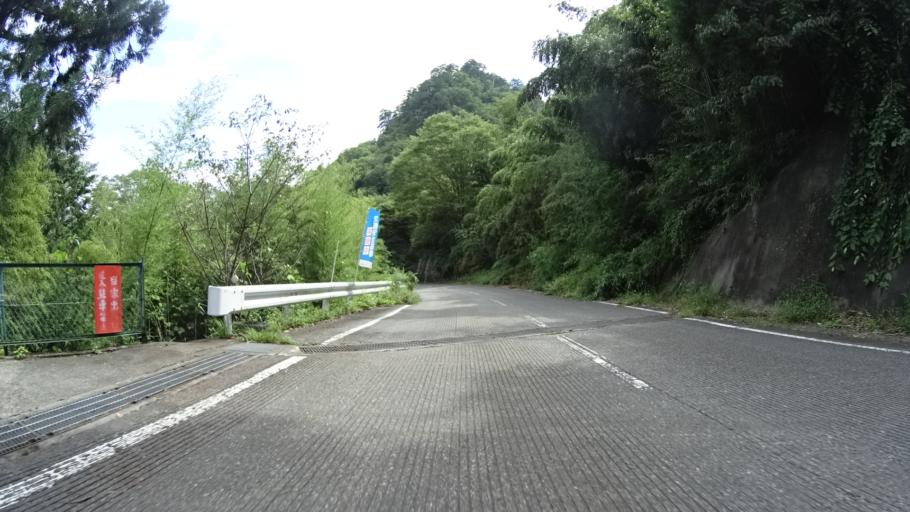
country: JP
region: Yamanashi
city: Kofu-shi
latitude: 35.7685
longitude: 138.5558
